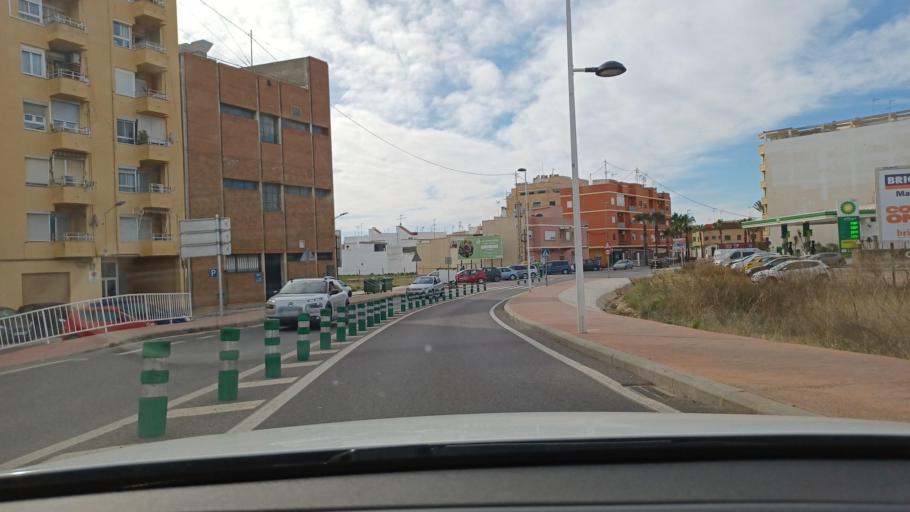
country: ES
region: Valencia
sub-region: Provincia de Valencia
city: Almussafes
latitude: 39.2896
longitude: -0.4200
